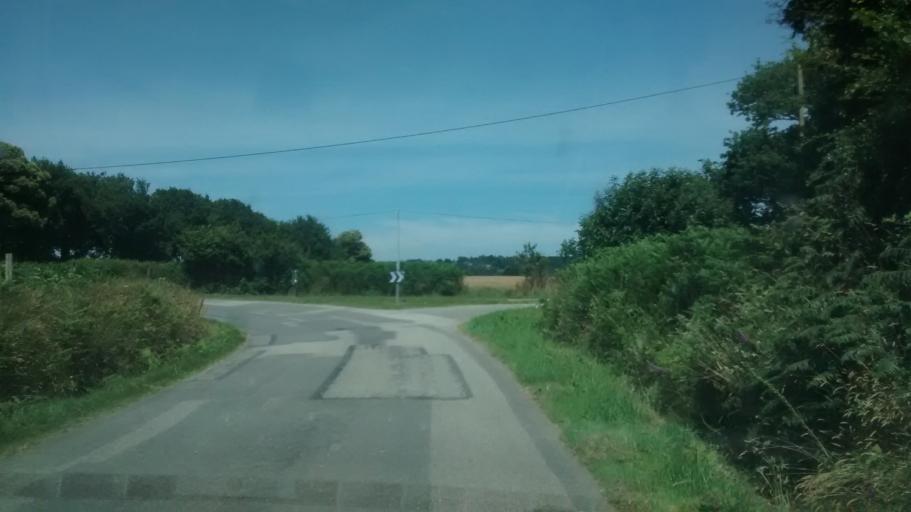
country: FR
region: Brittany
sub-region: Departement du Morbihan
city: Molac
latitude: 47.7190
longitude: -2.4601
